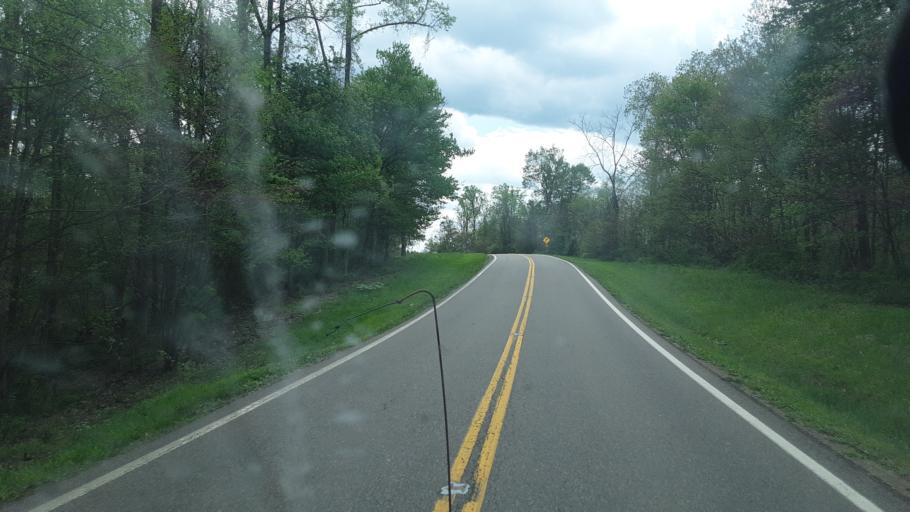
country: US
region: Ohio
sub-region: Noble County
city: Caldwell
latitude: 39.7347
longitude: -81.6483
